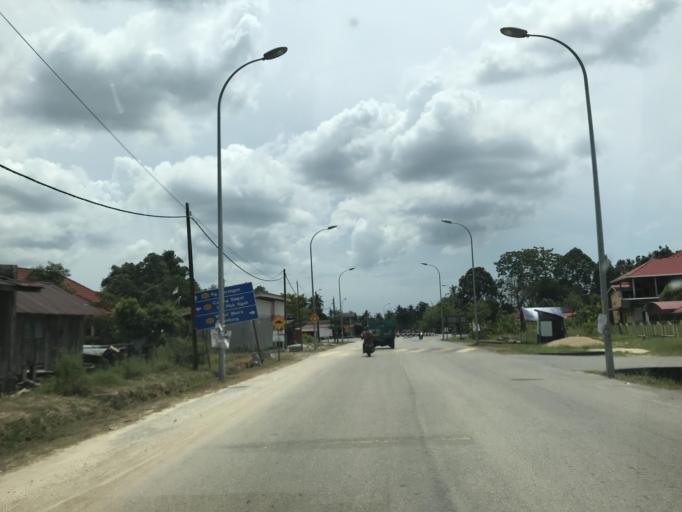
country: MY
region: Kelantan
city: Kota Bharu
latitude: 6.1439
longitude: 102.1865
